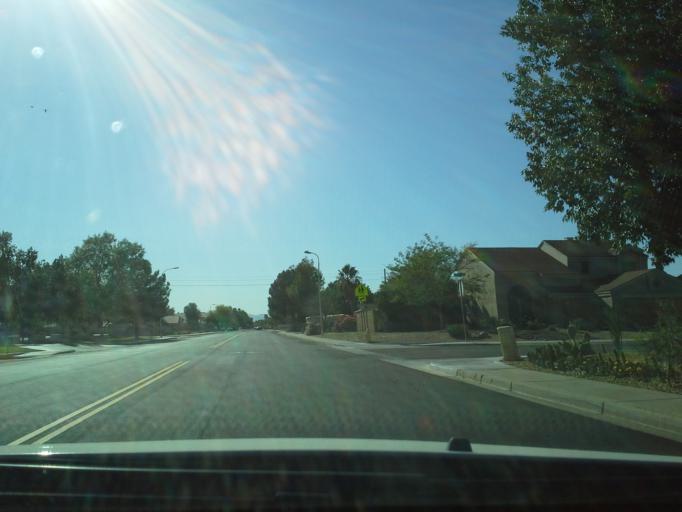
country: US
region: Arizona
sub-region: Maricopa County
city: Glendale
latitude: 33.5310
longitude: -112.2095
